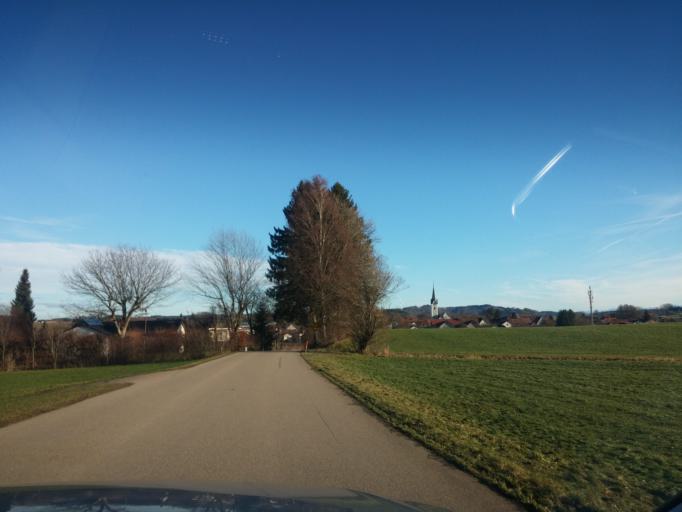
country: DE
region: Bavaria
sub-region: Swabia
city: Legau
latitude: 47.8577
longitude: 10.1224
